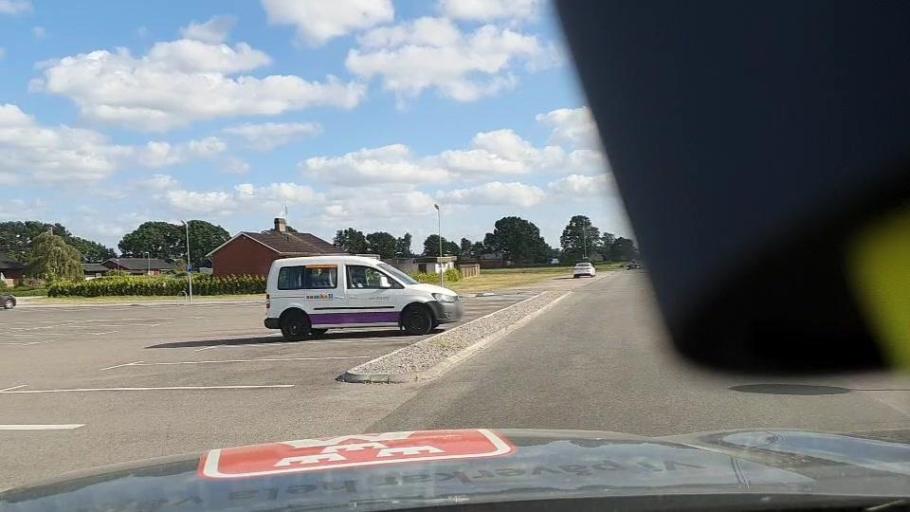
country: SE
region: Blekinge
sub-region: Solvesborgs Kommun
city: Soelvesborg
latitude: 56.0448
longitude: 14.6754
